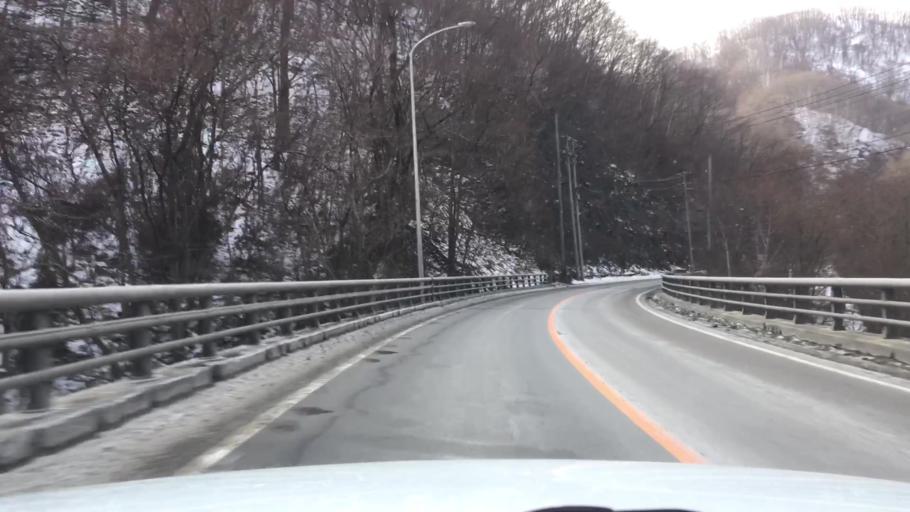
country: JP
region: Iwate
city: Tono
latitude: 39.6313
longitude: 141.5280
